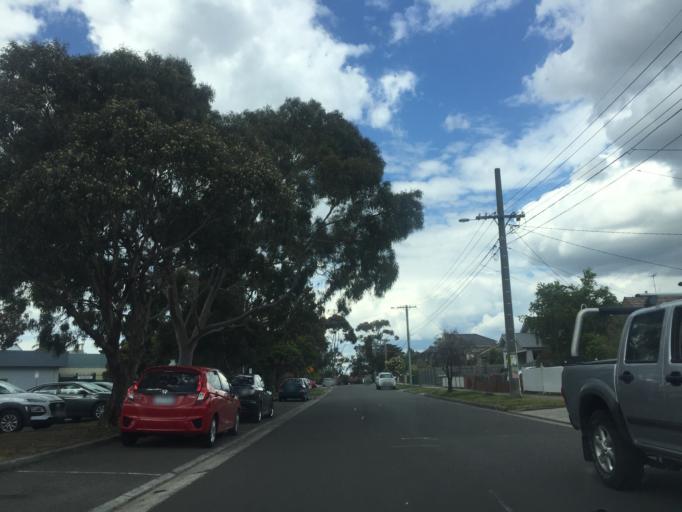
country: AU
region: Victoria
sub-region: Darebin
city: Kingsbury
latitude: -37.7170
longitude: 145.0183
